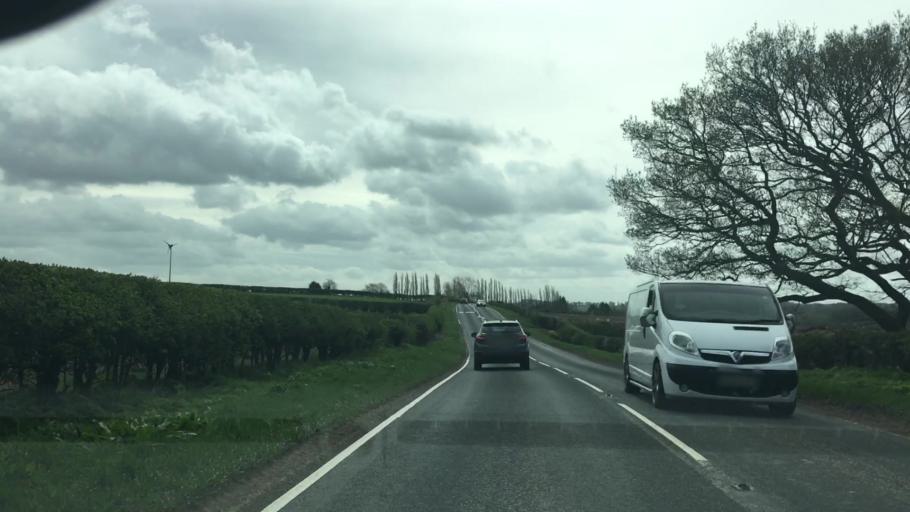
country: GB
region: England
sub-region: North Yorkshire
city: Knaresborough
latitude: 53.9614
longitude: -1.4454
